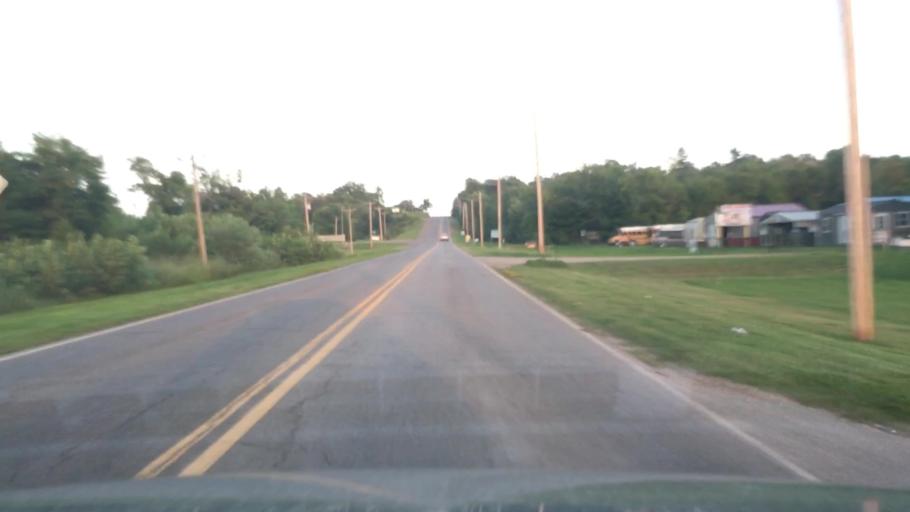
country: US
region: Oklahoma
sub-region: Cherokee County
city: Tahlequah
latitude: 35.9197
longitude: -94.9994
